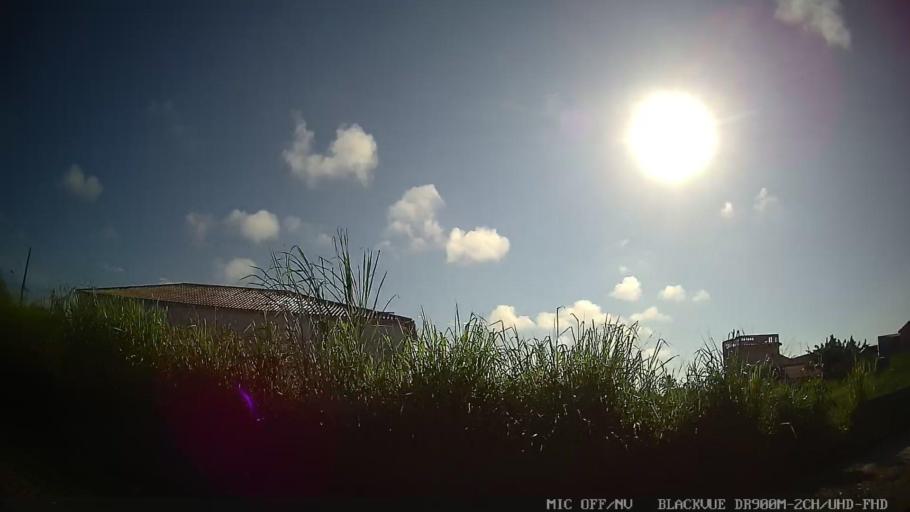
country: BR
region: Sao Paulo
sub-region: Peruibe
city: Peruibe
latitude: -24.2699
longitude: -46.9379
